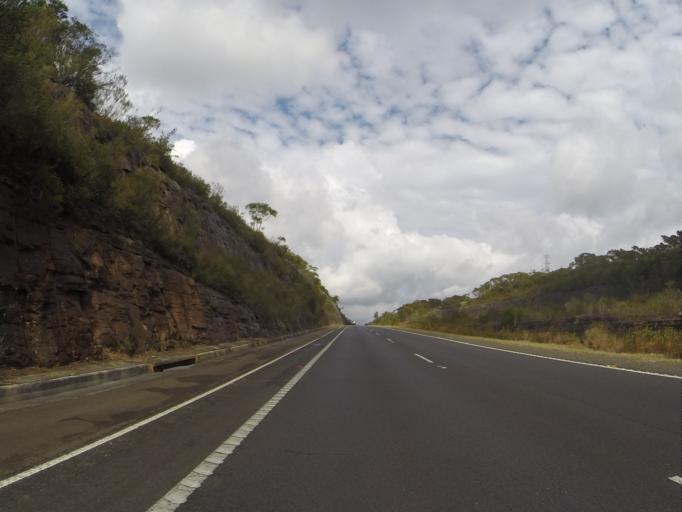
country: AU
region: New South Wales
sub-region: Wollongong
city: Helensburgh
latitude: -34.2189
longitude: 150.9548
